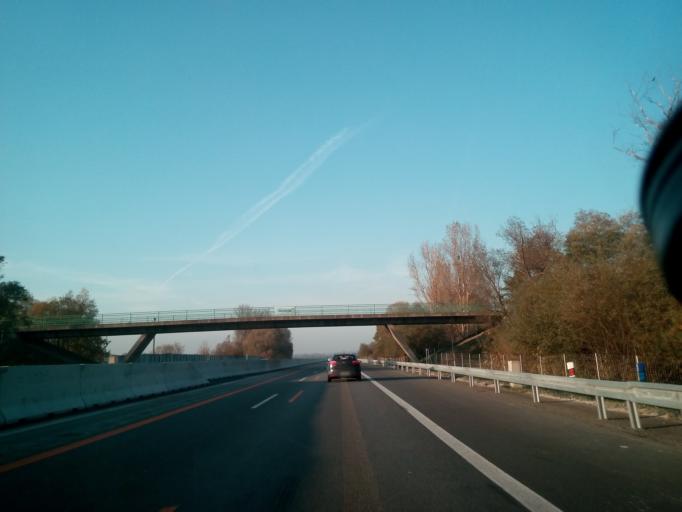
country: SK
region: Kosicky
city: Kosice
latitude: 48.7987
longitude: 21.3115
